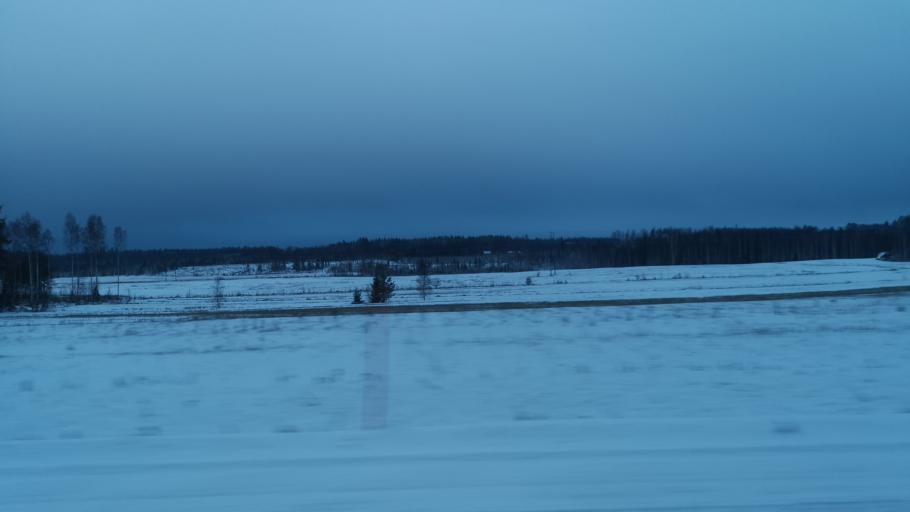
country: FI
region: Southern Savonia
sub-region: Savonlinna
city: Savonlinna
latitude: 61.9544
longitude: 28.8507
